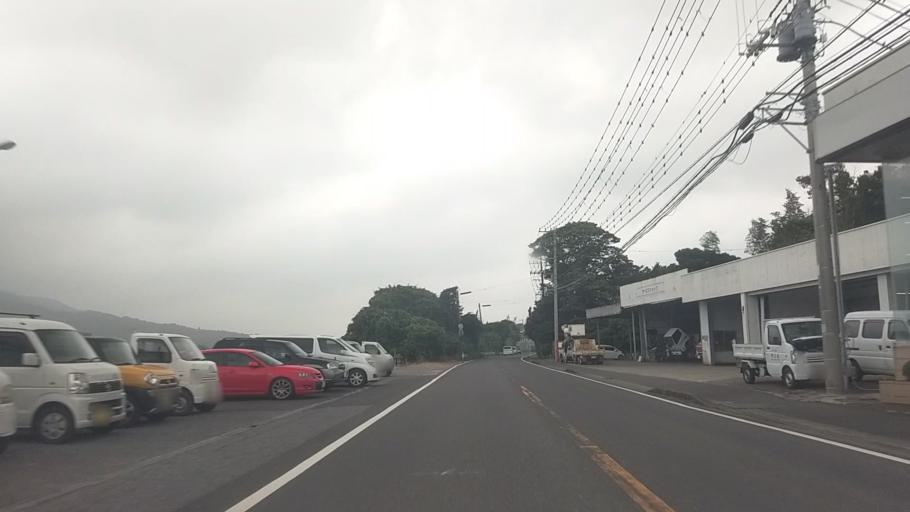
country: JP
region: Chiba
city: Kawaguchi
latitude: 35.1073
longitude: 140.0929
